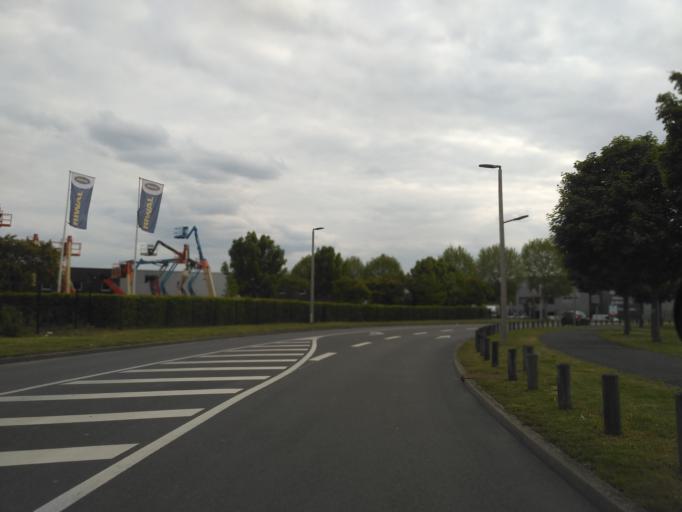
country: FR
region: Ile-de-France
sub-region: Departement de Seine-et-Marne
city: Vert-Saint-Denis
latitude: 48.5711
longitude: 2.6343
